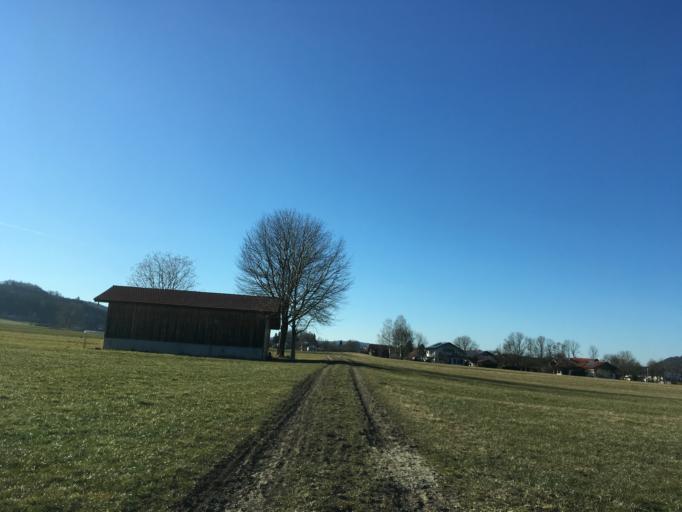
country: DE
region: Bavaria
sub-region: Upper Bavaria
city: Bruckmuhl
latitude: 47.8683
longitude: 11.9075
